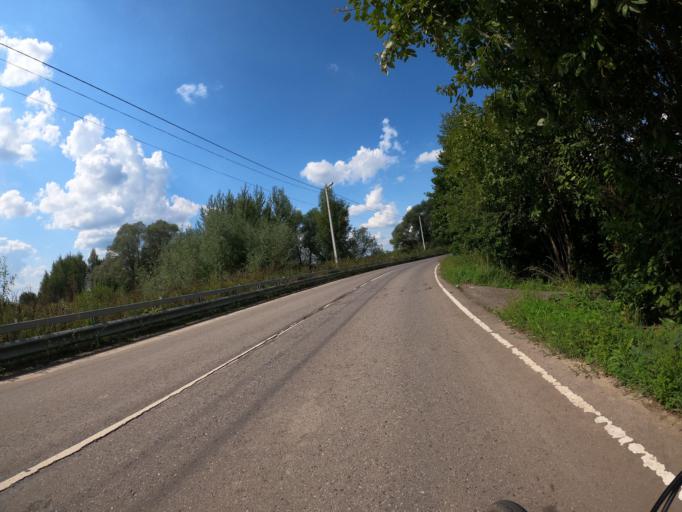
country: RU
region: Moskovskaya
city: Troitskoye
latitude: 55.2460
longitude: 38.5772
